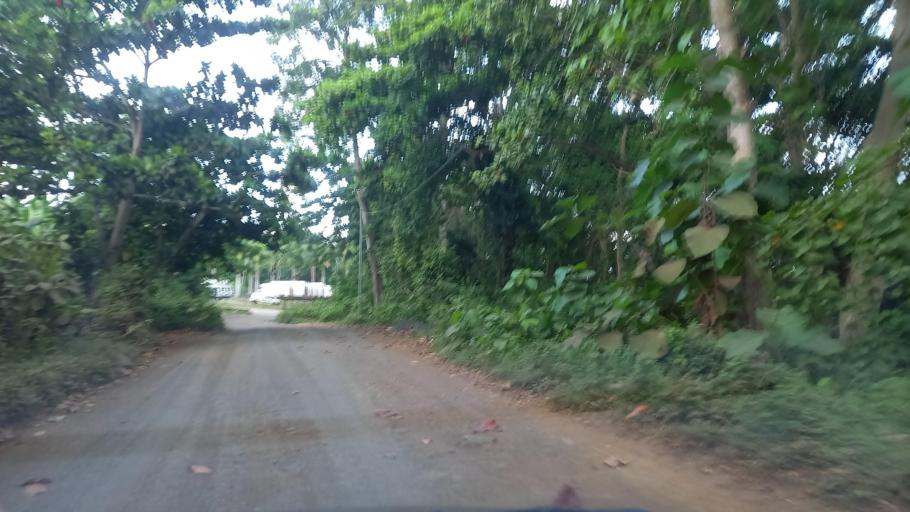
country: YT
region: Dembeni
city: Dembeni
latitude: -12.8285
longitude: 45.1919
